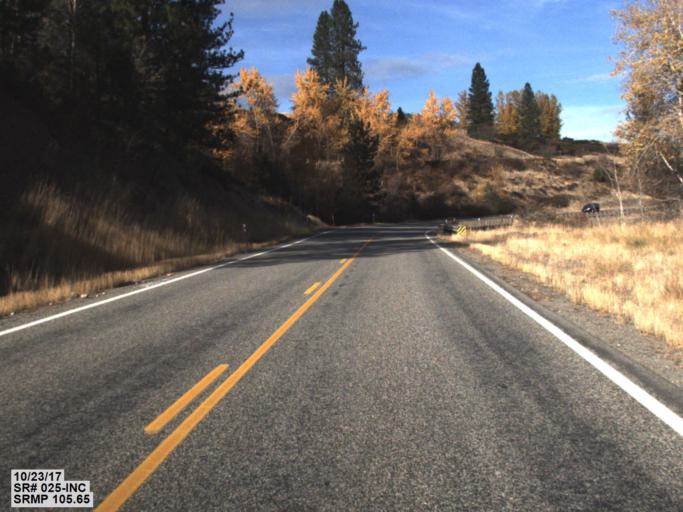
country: CA
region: British Columbia
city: Rossland
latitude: 48.8499
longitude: -117.8968
